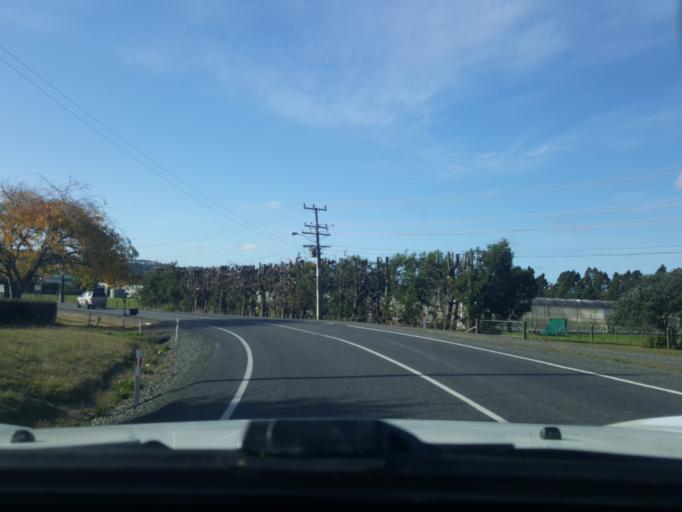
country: NZ
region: Auckland
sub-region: Auckland
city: Muriwai Beach
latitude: -36.7692
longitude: 174.5757
